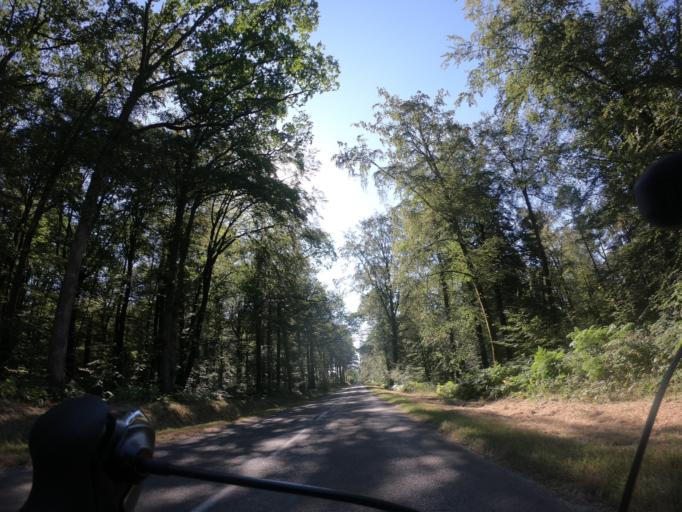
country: FR
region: Lower Normandy
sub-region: Departement de l'Orne
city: Tesse-la-Madeleine
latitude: 48.5681
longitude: -0.4428
